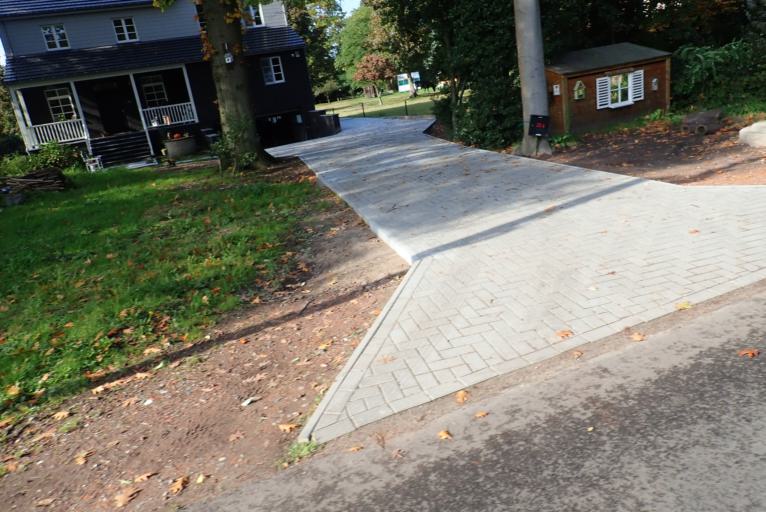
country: BE
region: Flanders
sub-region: Provincie Antwerpen
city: Kalmthout
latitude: 51.3961
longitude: 4.4663
